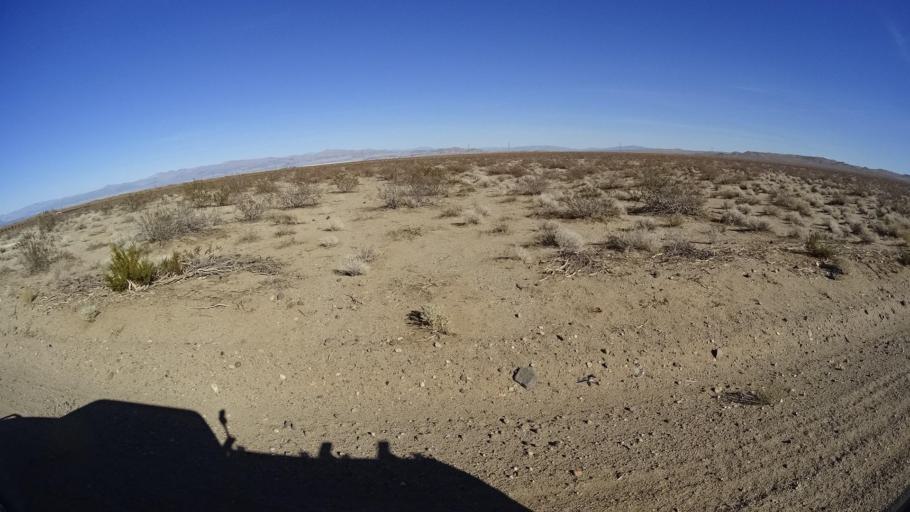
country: US
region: California
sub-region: Kern County
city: China Lake Acres
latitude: 35.5865
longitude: -117.7908
